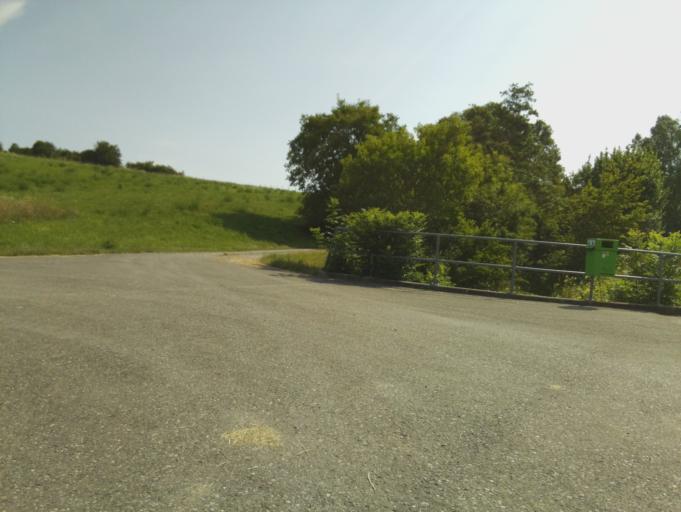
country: CH
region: Zurich
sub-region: Bezirk Andelfingen
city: Grossandelfingen
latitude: 47.5779
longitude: 8.6740
